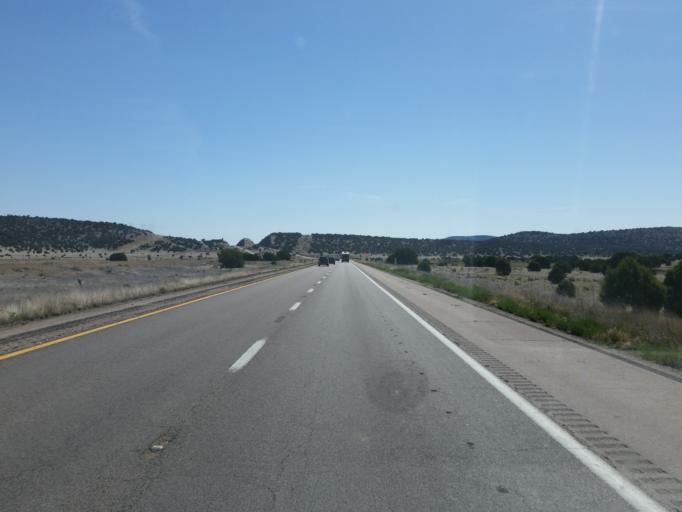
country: US
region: Arizona
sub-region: Mohave County
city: Peach Springs
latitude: 35.2314
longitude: -113.2191
